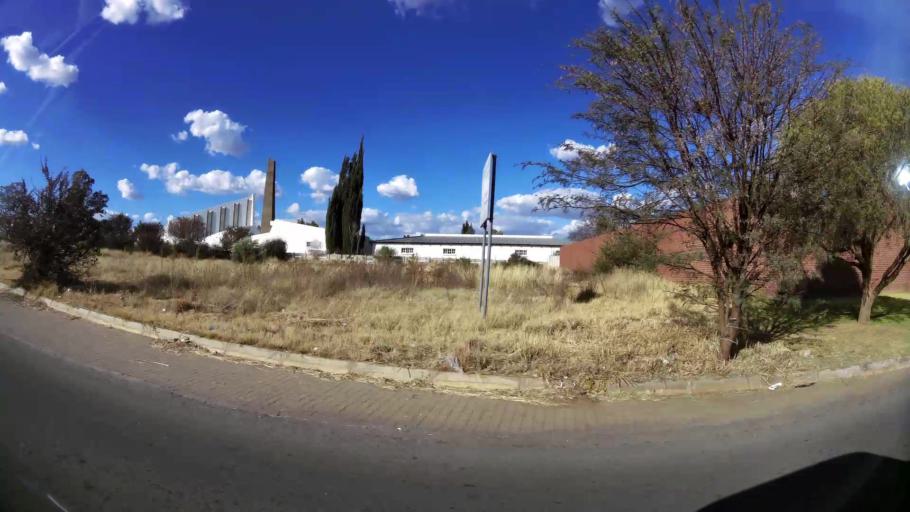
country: ZA
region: North-West
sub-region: Dr Kenneth Kaunda District Municipality
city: Klerksdorp
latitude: -26.8533
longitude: 26.6772
